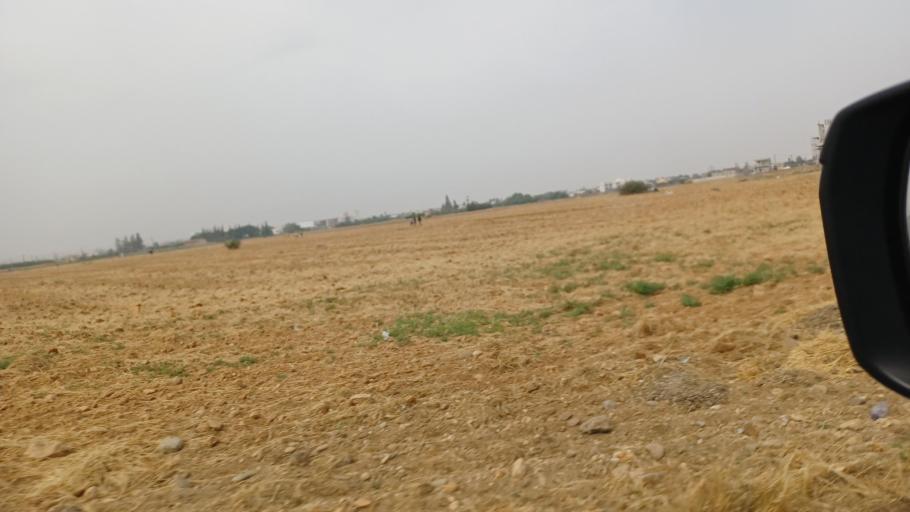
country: CY
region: Lefkosia
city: Kokkinotrimithia
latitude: 35.1544
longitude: 33.2191
